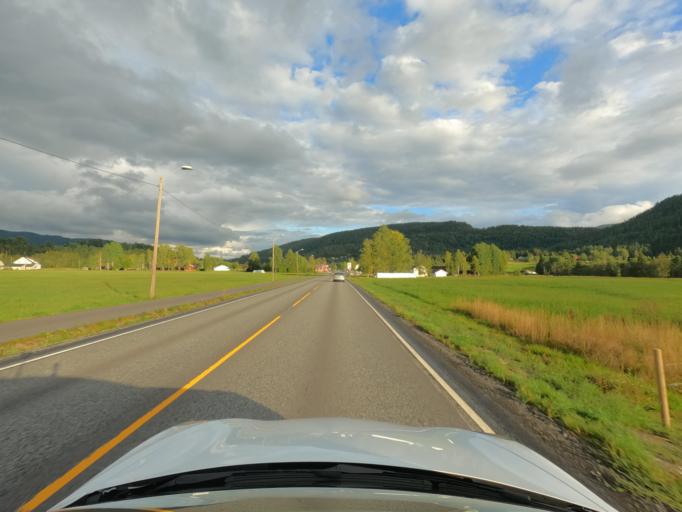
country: NO
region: Telemark
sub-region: Hjartdal
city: Sauland
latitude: 59.6150
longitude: 8.9435
